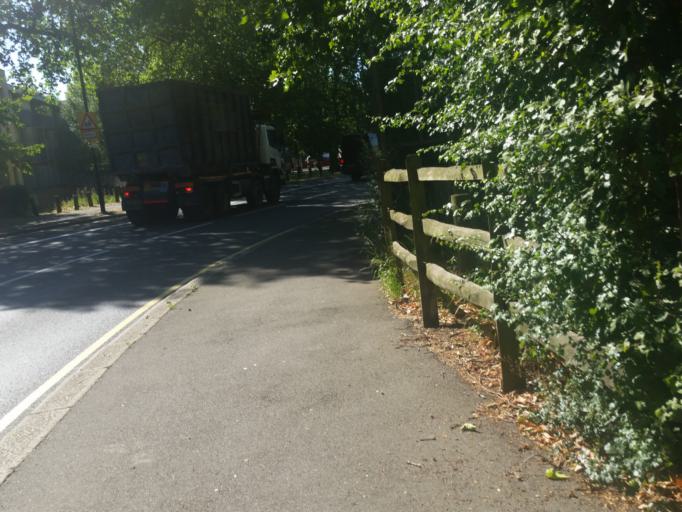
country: GB
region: England
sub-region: Greater London
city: Hammersmith
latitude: 51.5202
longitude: -0.2284
